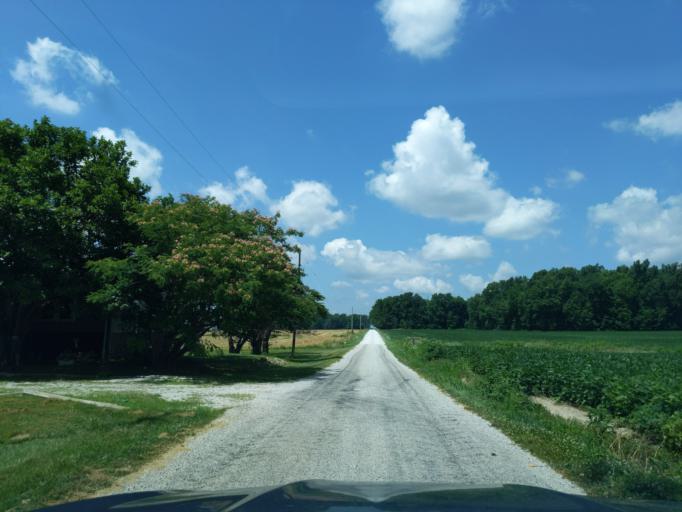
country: US
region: Indiana
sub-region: Ripley County
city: Osgood
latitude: 39.2210
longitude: -85.3514
